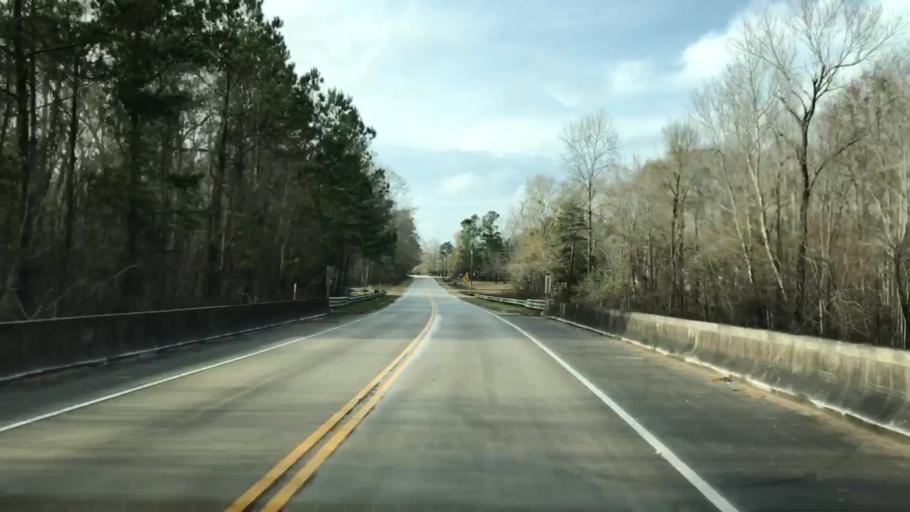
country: US
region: South Carolina
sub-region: Williamsburg County
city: Andrews
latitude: 33.4996
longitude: -79.5138
